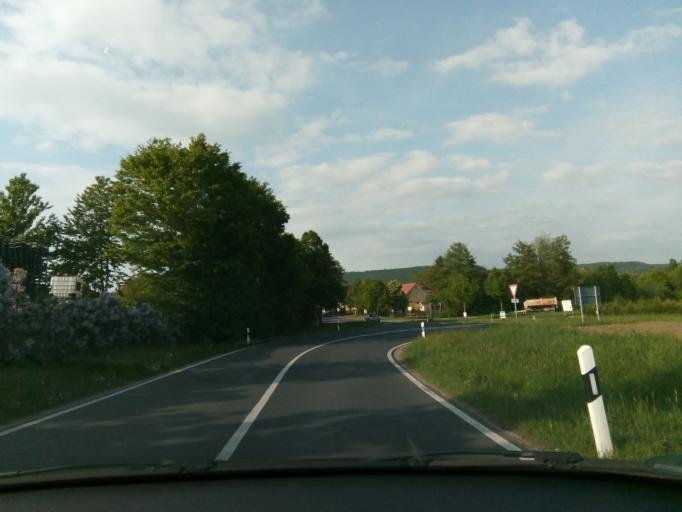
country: DE
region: Bavaria
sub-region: Regierungsbezirk Unterfranken
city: Oberschwarzach
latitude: 49.8571
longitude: 10.4101
